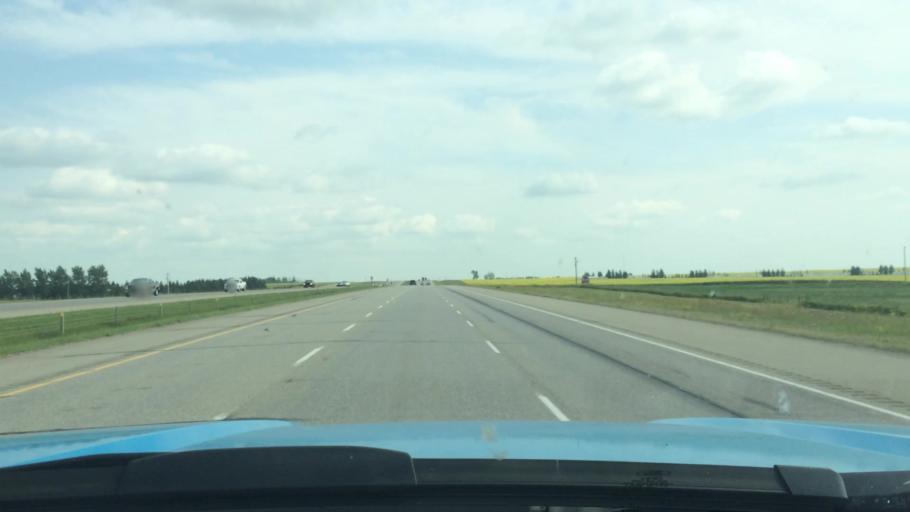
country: CA
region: Alberta
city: Crossfield
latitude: 51.4553
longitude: -114.0192
